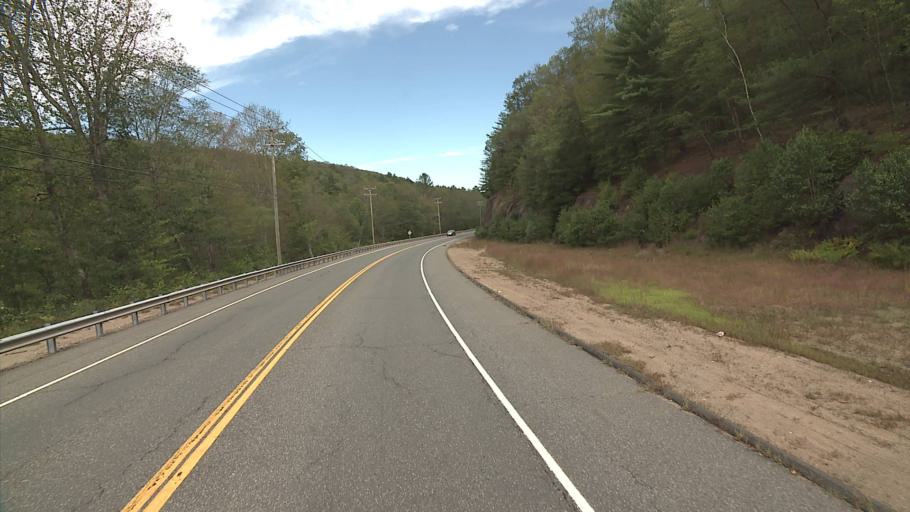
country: US
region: Connecticut
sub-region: Tolland County
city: Stafford Springs
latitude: 41.9124
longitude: -72.2964
